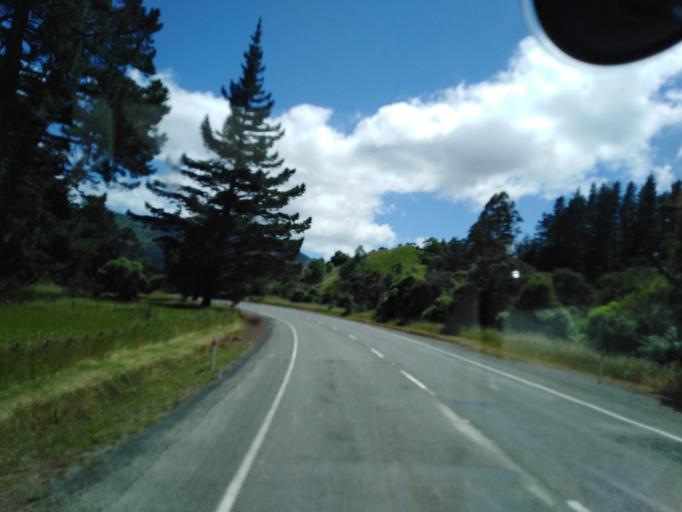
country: NZ
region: Nelson
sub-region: Nelson City
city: Nelson
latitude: -41.2208
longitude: 173.3978
